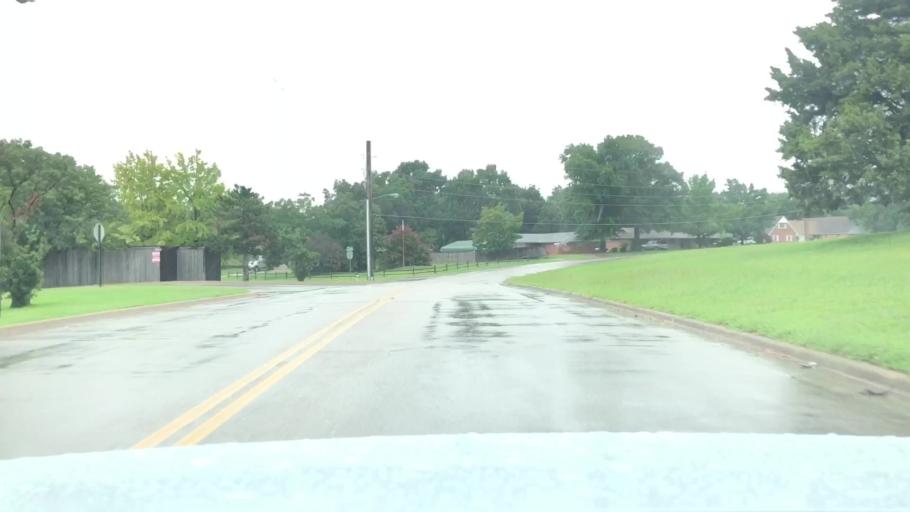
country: US
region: Oklahoma
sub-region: Washington County
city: Bartlesville
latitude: 36.7386
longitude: -95.9317
